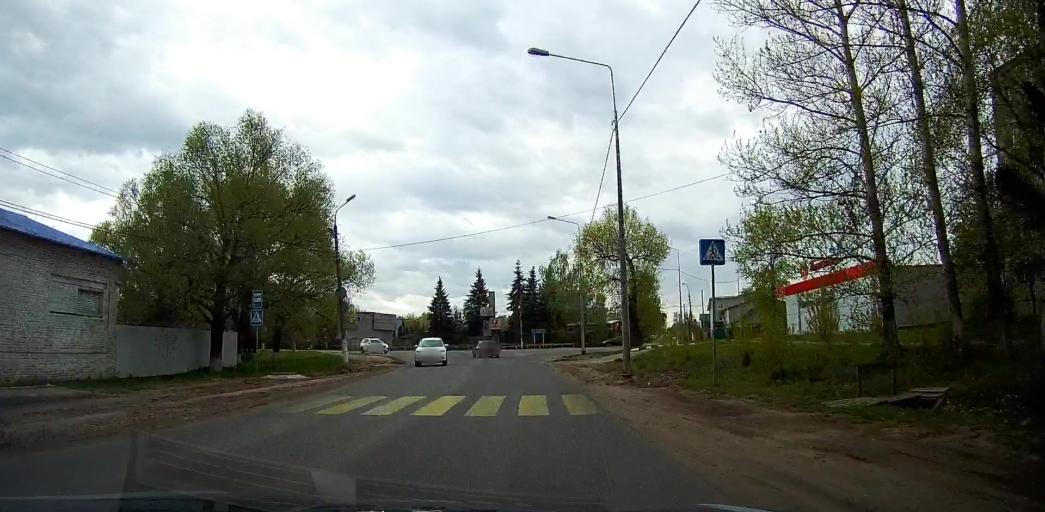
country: RU
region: Moskovskaya
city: Pavlovskiy Posad
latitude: 55.7738
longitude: 38.6863
